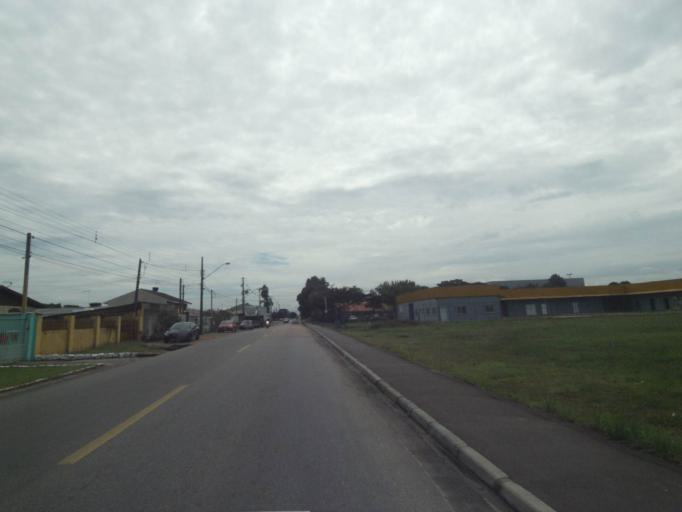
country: BR
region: Parana
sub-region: Pinhais
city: Pinhais
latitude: -25.4808
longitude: -49.1945
